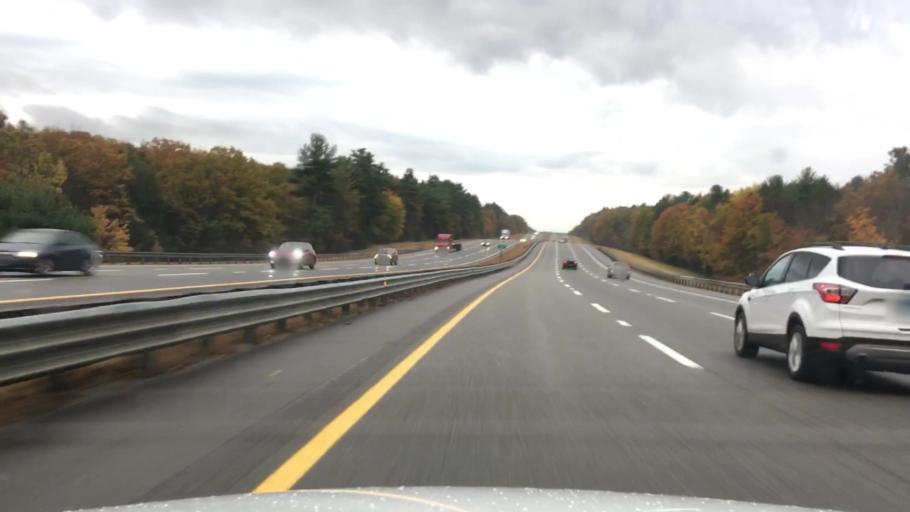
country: US
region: Maine
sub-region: York County
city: Cape Neddick
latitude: 43.2225
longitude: -70.6375
